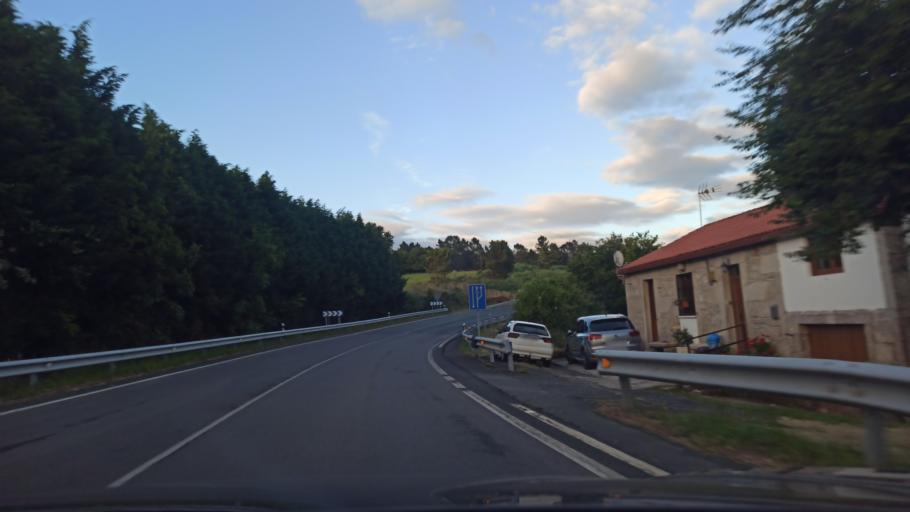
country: ES
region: Galicia
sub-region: Provincia de Pontevedra
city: Rodeiro
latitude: 42.7688
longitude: -7.9811
